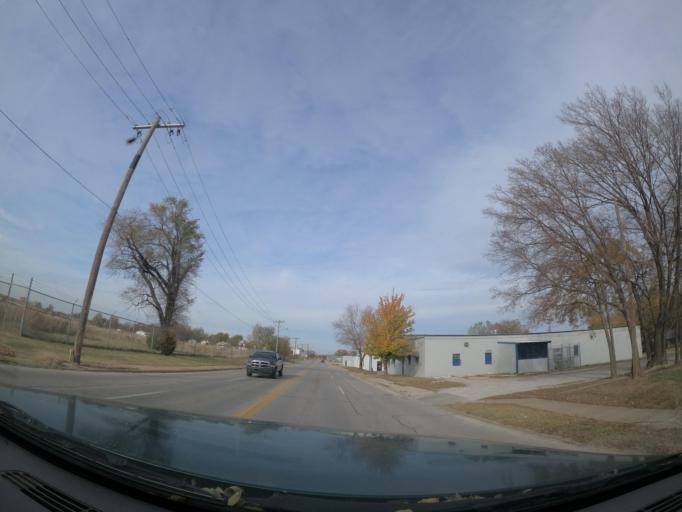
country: US
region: Oklahoma
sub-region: Tulsa County
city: Tulsa
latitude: 36.1699
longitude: -95.9671
